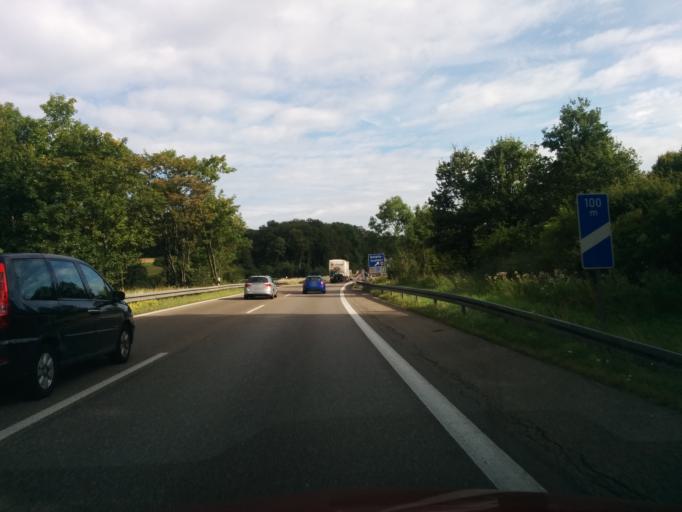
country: DE
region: Baden-Wuerttemberg
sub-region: Regierungsbezirk Stuttgart
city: Hohenstadt
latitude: 48.5441
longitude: 9.6477
